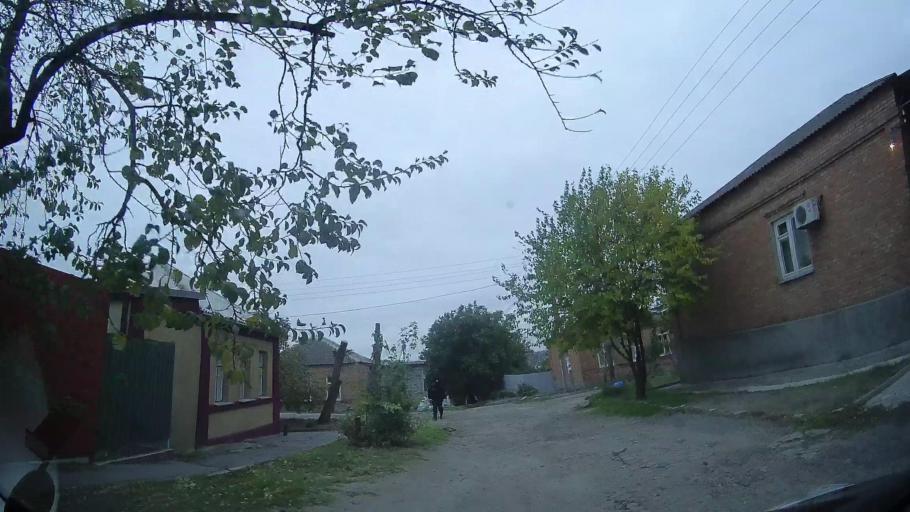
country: RU
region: Rostov
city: Severnyy
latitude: 47.2684
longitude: 39.6773
